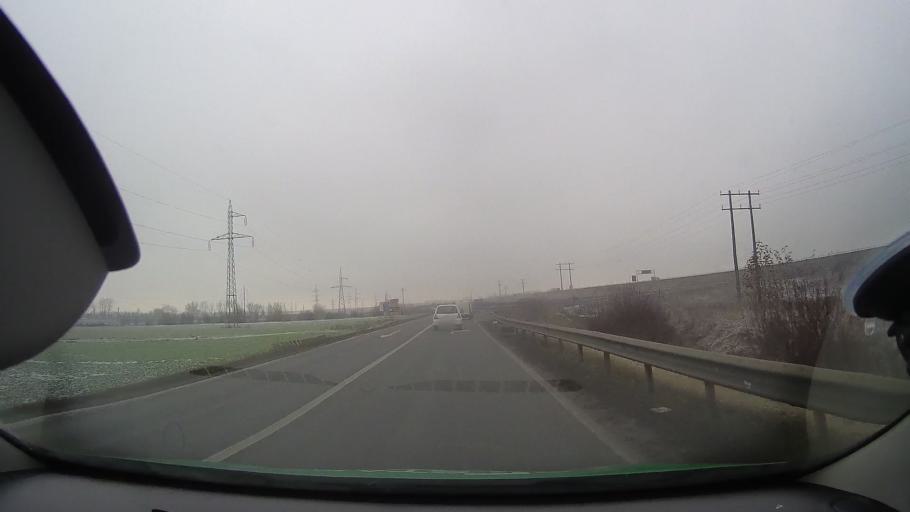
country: RO
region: Cluj
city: Turda
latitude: 46.5492
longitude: 23.7720
